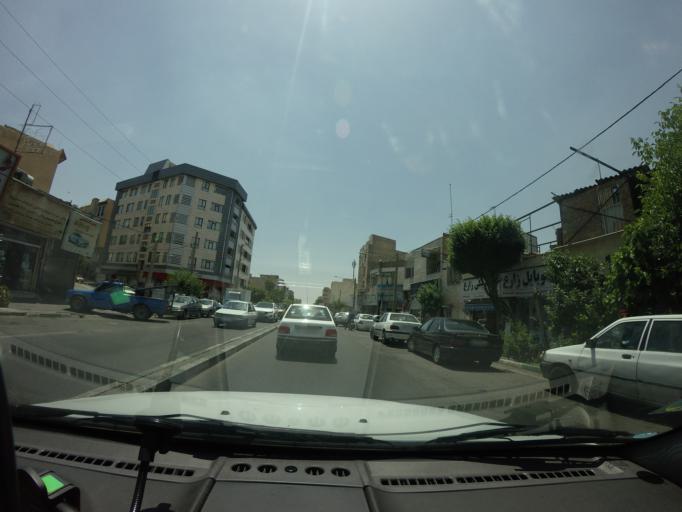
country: IR
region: Tehran
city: Tajrish
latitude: 35.7625
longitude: 51.2842
